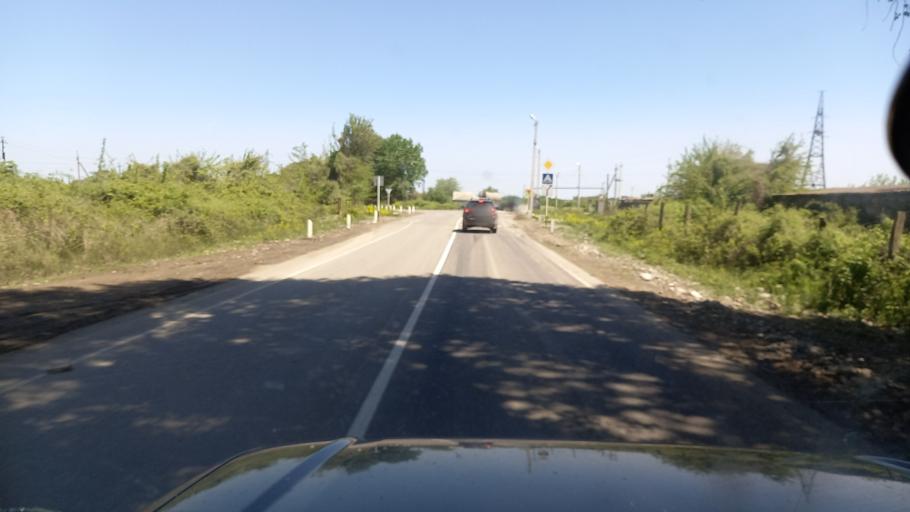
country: RU
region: Dagestan
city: Samur
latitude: 41.8031
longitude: 48.5015
